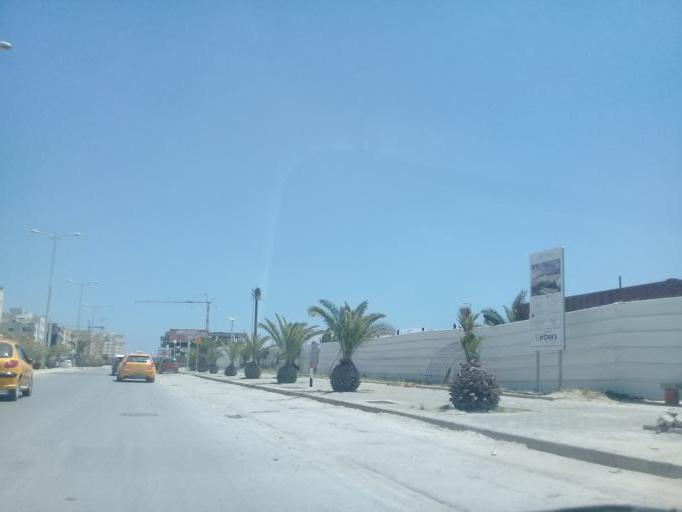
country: TN
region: Tunis
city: La Goulette
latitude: 36.8424
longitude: 10.2748
